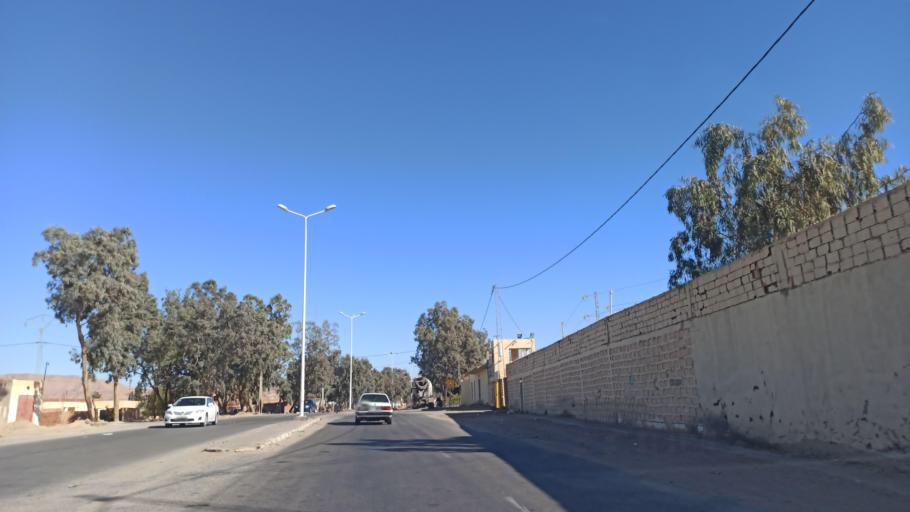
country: TN
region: Gafsa
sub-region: Gafsa Municipality
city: Gafsa
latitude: 34.4003
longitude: 8.7230
